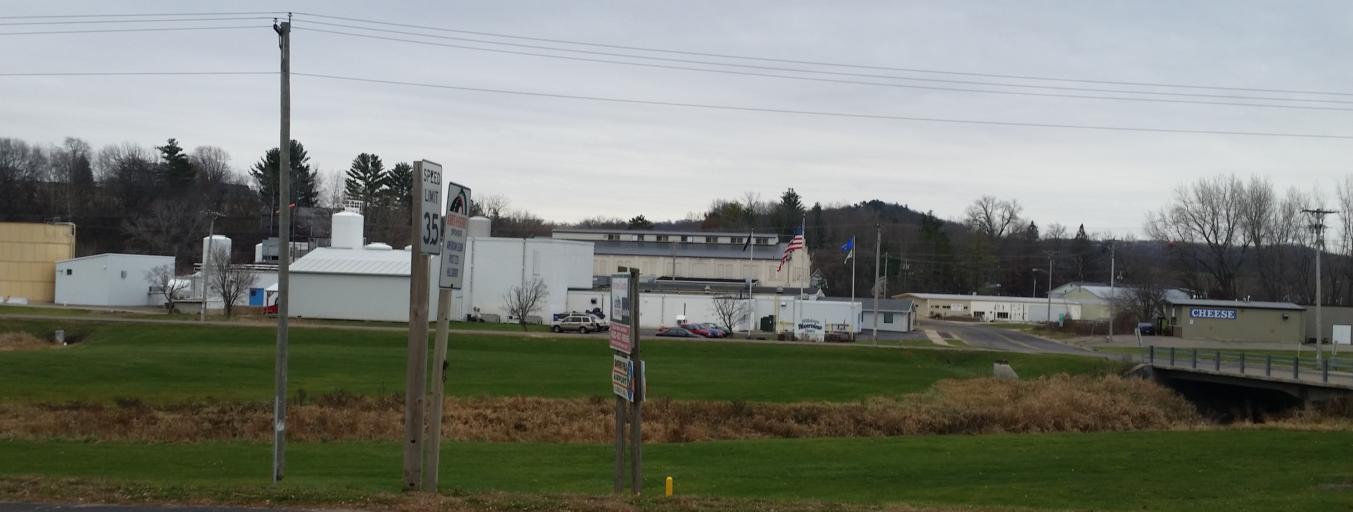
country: US
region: Wisconsin
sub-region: Vernon County
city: Hillsboro
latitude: 43.6540
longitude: -90.3363
